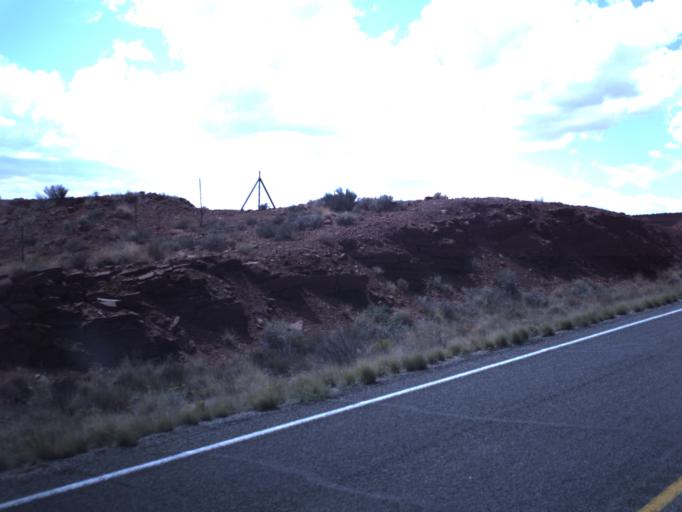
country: US
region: Utah
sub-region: San Juan County
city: Blanding
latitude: 37.2131
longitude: -109.8447
